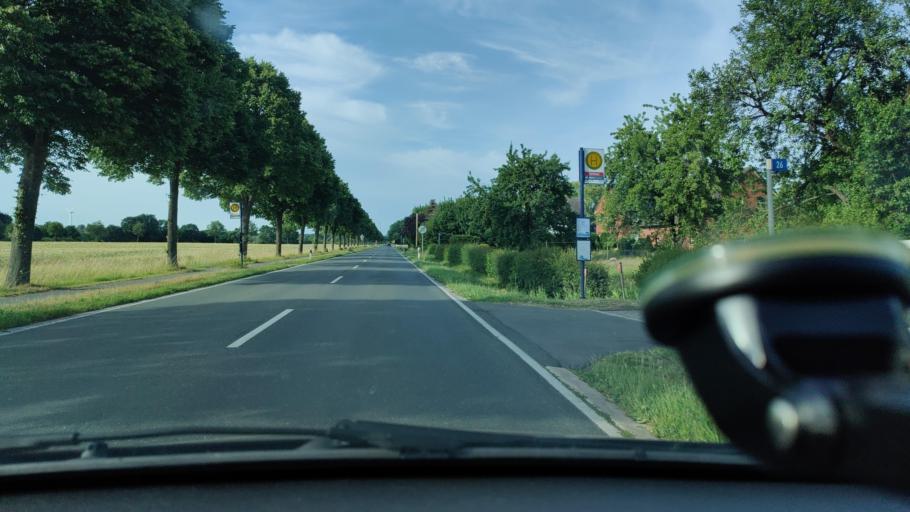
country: DE
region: North Rhine-Westphalia
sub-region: Regierungsbezirk Munster
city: Coesfeld
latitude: 51.9661
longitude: 7.1871
